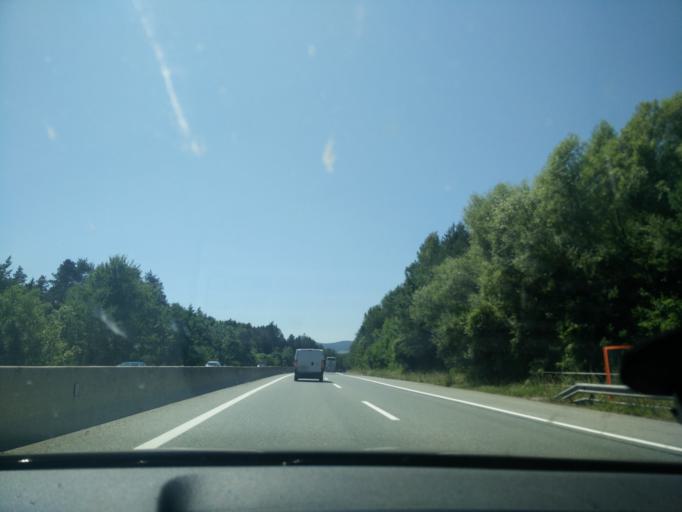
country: AT
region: Lower Austria
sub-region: Politischer Bezirk Neunkirchen
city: Seebenstein
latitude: 47.6954
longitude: 16.1301
